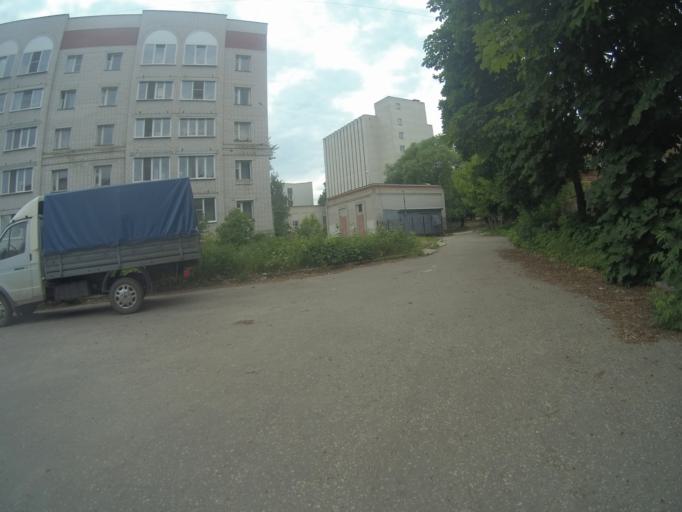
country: RU
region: Vladimir
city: Vladimir
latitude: 56.1392
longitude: 40.3938
